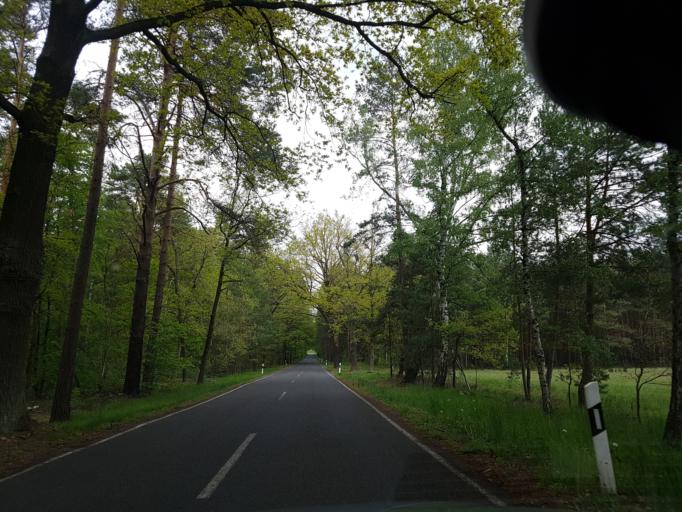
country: DE
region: Brandenburg
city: Crinitz
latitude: 51.7558
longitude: 13.7521
